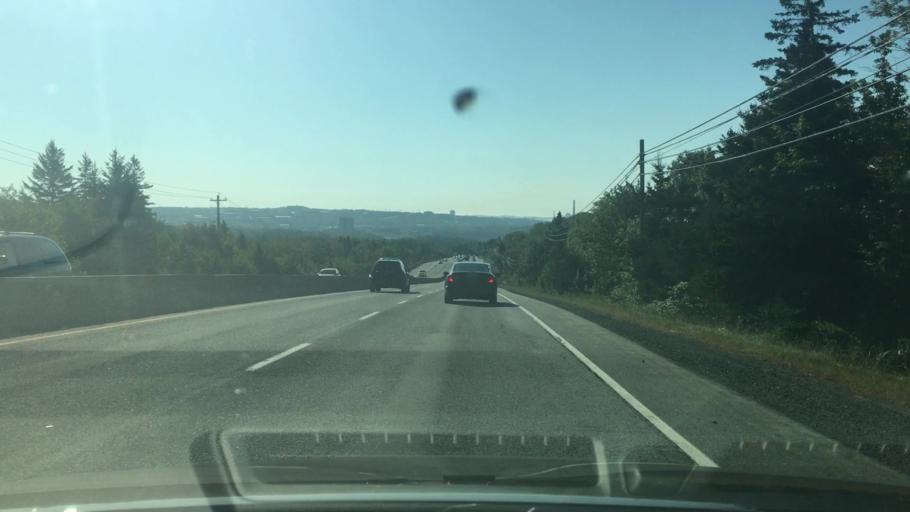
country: CA
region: Nova Scotia
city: Dartmouth
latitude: 44.7159
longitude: -63.6327
